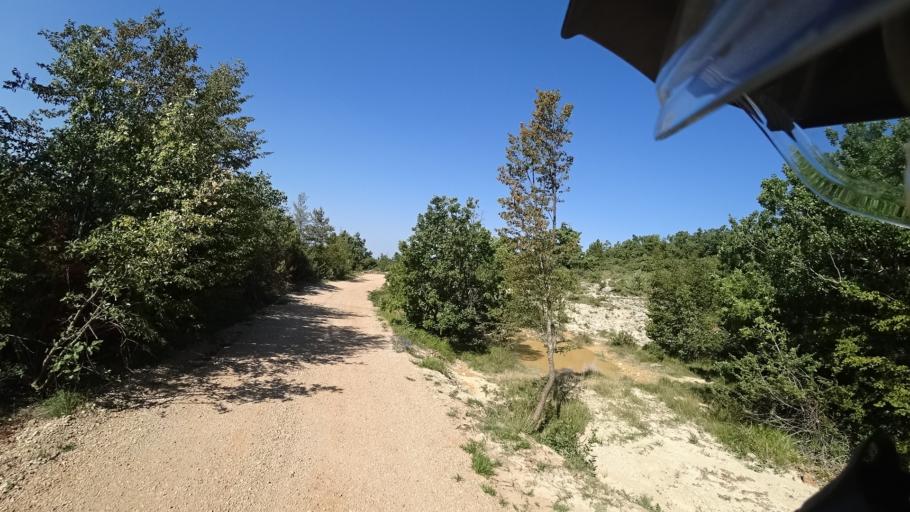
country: HR
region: Sibensko-Kniniska
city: Drnis
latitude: 43.9011
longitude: 16.1765
